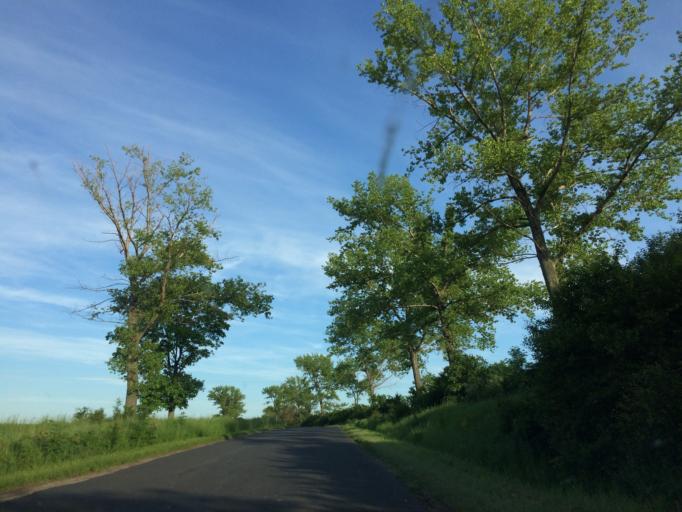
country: PL
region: Lower Silesian Voivodeship
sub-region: Powiat dzierzoniowski
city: Pieszyce
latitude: 50.7604
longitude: 16.5143
